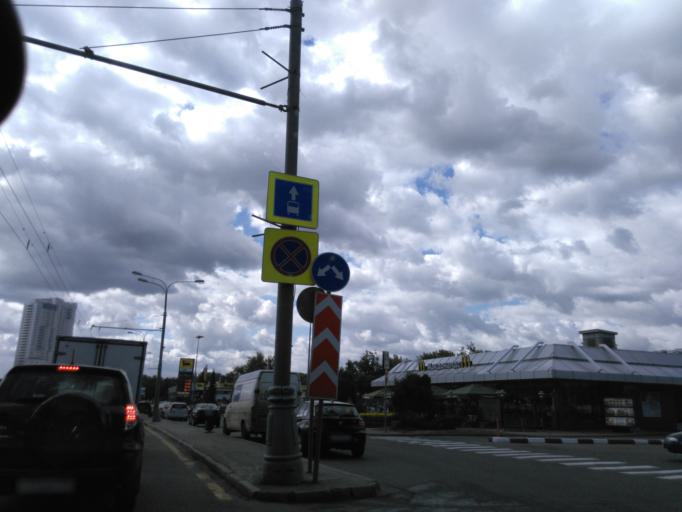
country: RU
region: Moskovskaya
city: Levoberezhnyy
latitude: 55.8661
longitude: 37.4625
